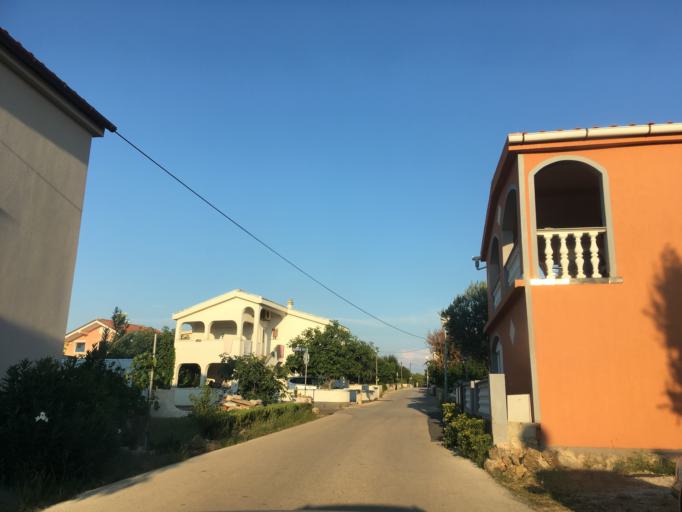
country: HR
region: Zadarska
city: Vir
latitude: 44.3050
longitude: 15.0949
